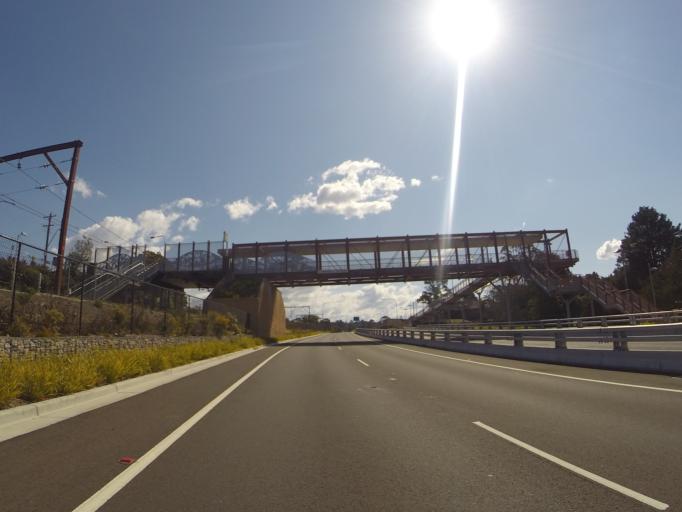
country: AU
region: New South Wales
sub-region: Blue Mountains Municipality
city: Hazelbrook
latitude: -33.7238
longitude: 150.4547
